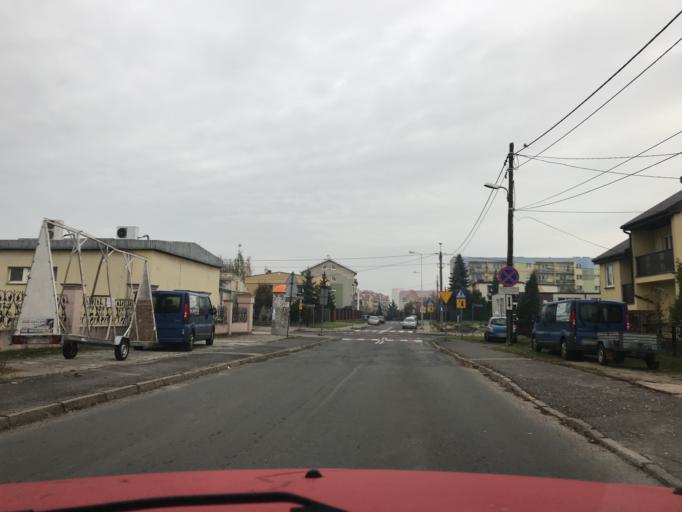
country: PL
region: Greater Poland Voivodeship
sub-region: Kalisz
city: Kalisz
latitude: 51.7571
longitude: 18.0678
